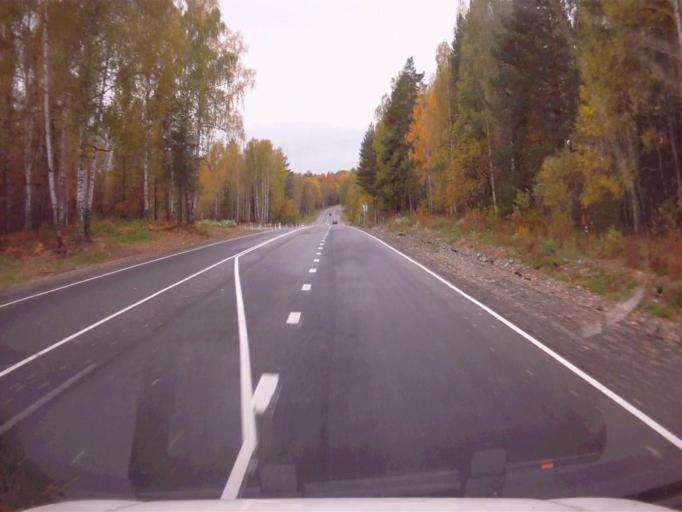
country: RU
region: Chelyabinsk
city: Nyazepetrovsk
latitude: 56.0673
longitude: 59.6965
